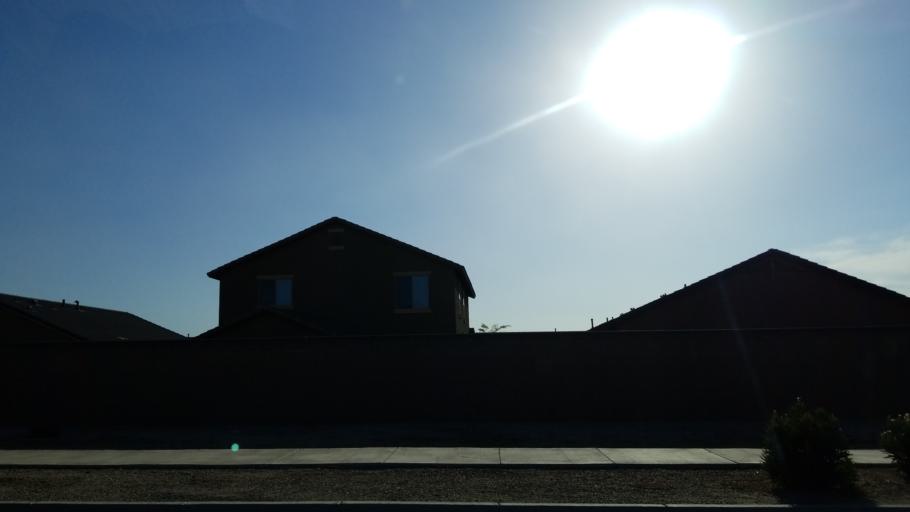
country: US
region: Arizona
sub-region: Maricopa County
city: Laveen
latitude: 33.3821
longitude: -112.2199
